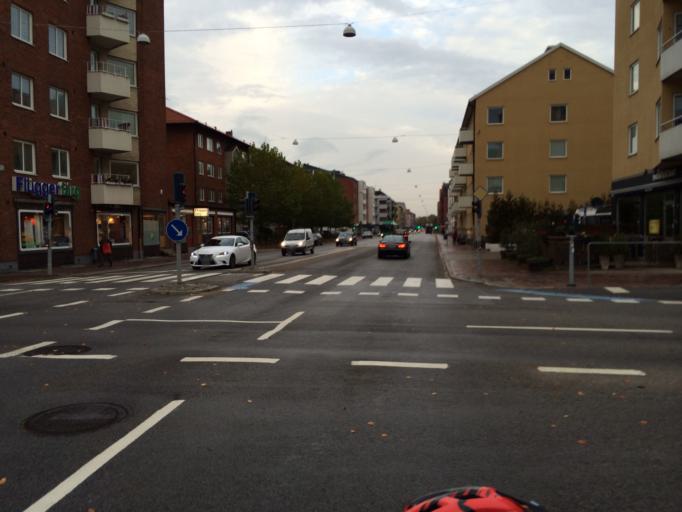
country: SE
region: Skane
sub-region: Malmo
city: Malmoe
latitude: 55.5936
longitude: 12.9836
